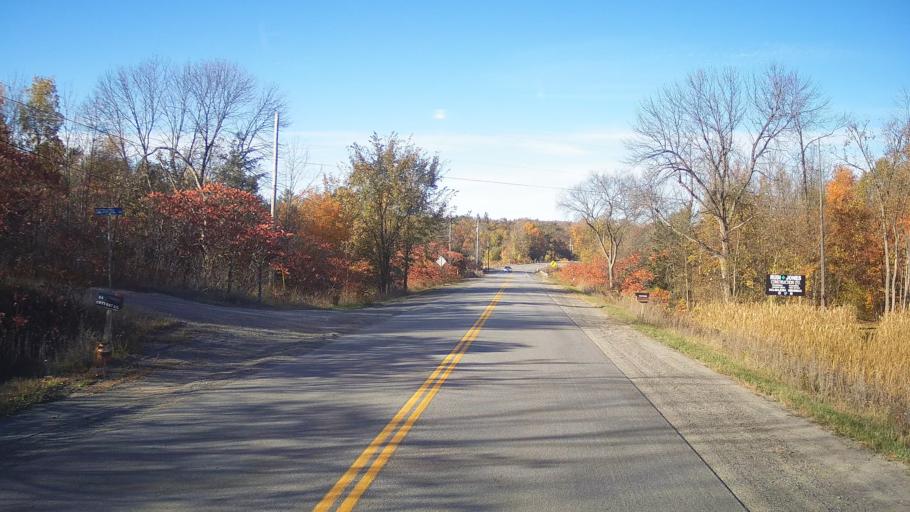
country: CA
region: Ontario
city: Gananoque
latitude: 44.5830
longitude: -76.4204
